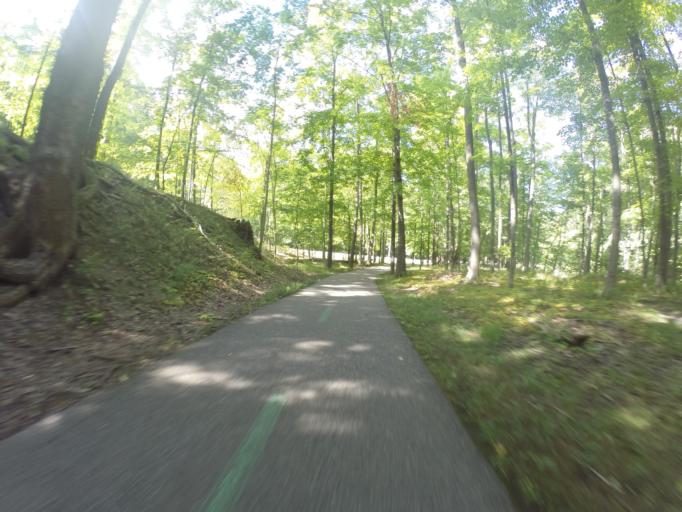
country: US
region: Ohio
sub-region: Cuyahoga County
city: Richmond Heights
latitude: 41.5516
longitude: -81.5298
